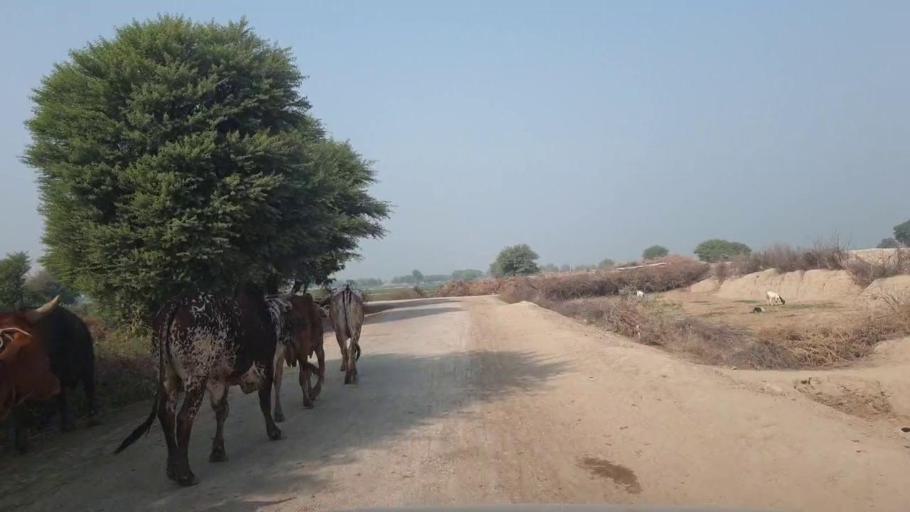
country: PK
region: Sindh
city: Hala
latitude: 25.8213
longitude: 68.4091
